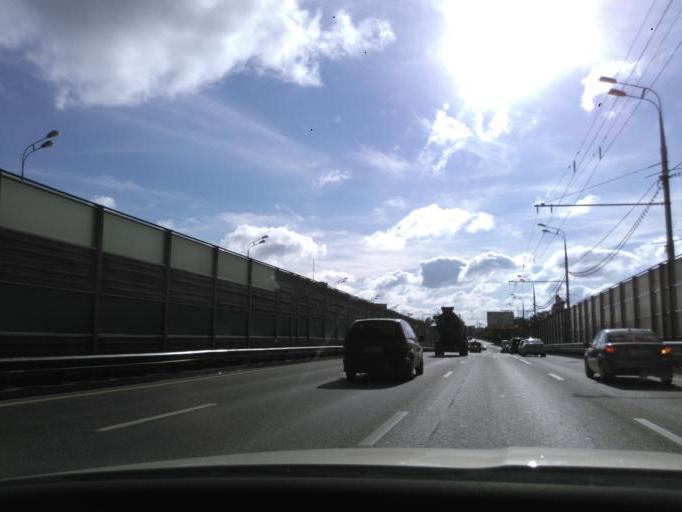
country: RU
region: Moscow
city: Mar'ina Roshcha
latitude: 55.7912
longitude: 37.6339
